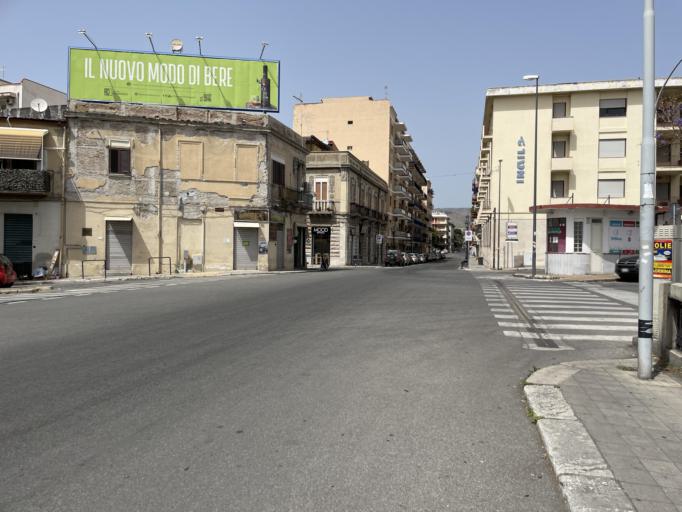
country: IT
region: Calabria
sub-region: Provincia di Reggio Calabria
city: Reggio Calabria
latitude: 38.1014
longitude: 15.6357
